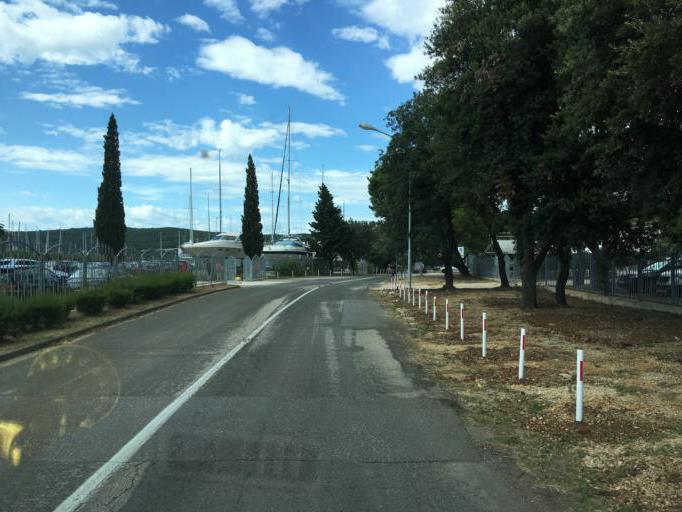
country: HR
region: Primorsko-Goranska
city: Punat
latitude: 45.0299
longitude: 14.6290
